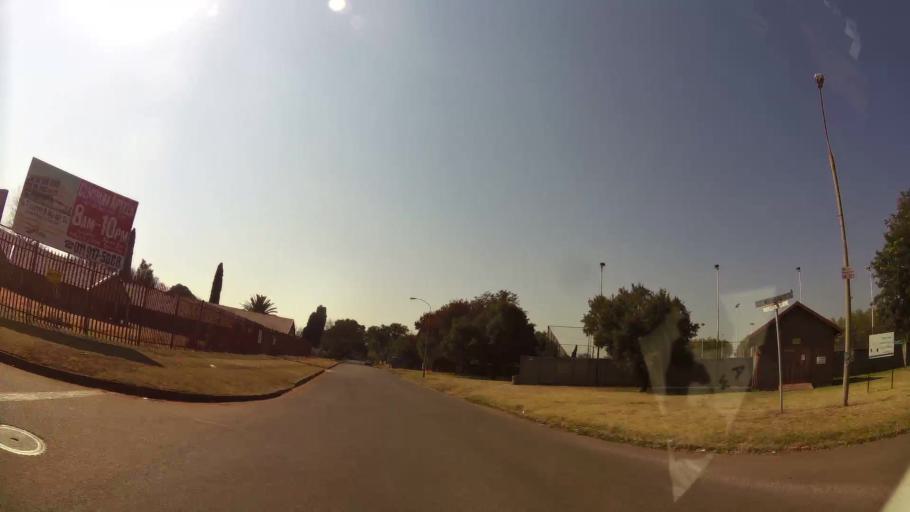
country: ZA
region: Gauteng
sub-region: Ekurhuleni Metropolitan Municipality
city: Boksburg
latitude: -26.2456
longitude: 28.2646
